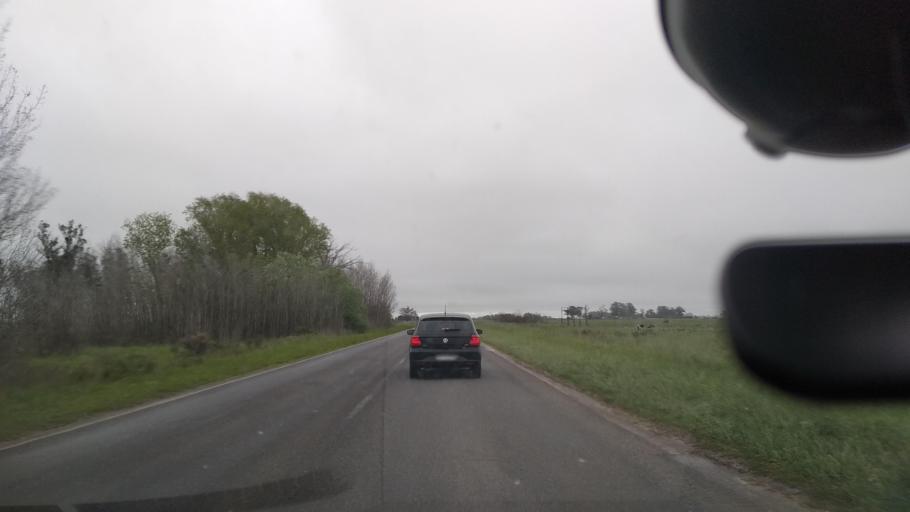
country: AR
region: Buenos Aires
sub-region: Partido de Magdalena
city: Magdalena
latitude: -35.2271
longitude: -57.7204
